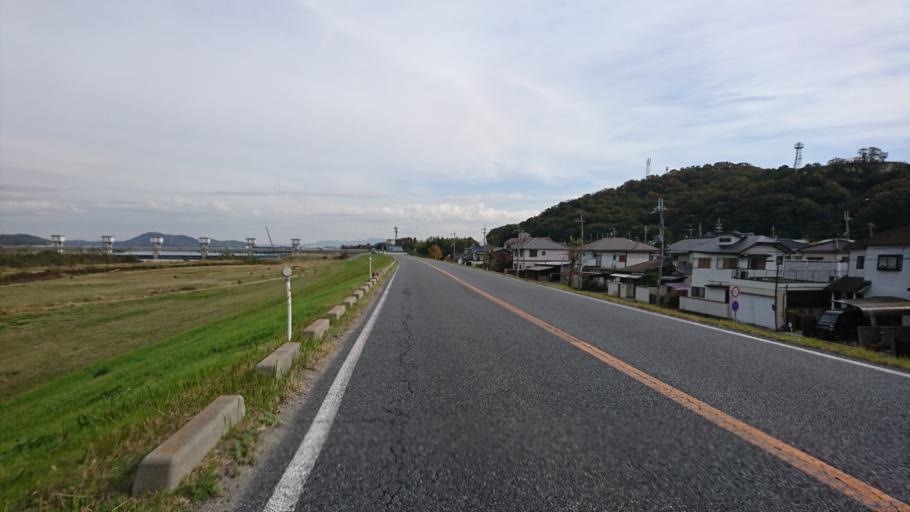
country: JP
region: Hyogo
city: Kakogawacho-honmachi
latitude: 34.7931
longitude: 134.8825
